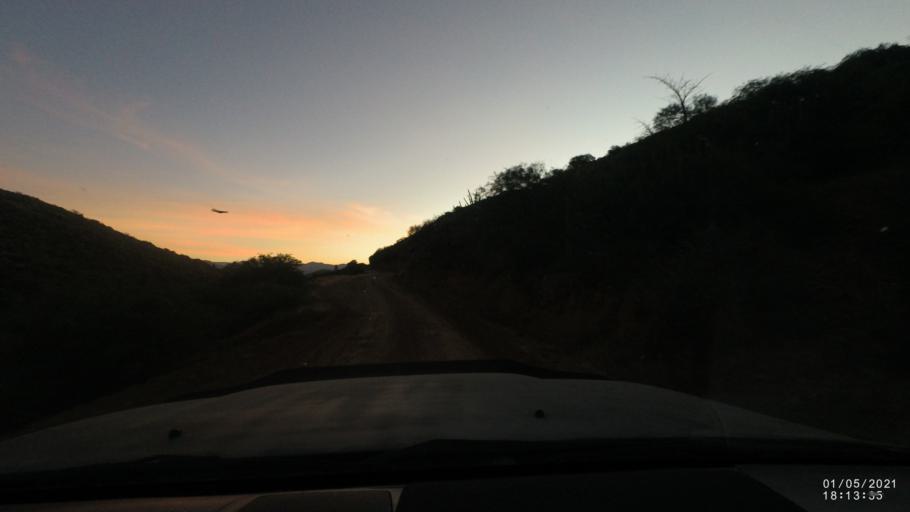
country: BO
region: Cochabamba
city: Capinota
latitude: -17.6744
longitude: -66.2071
